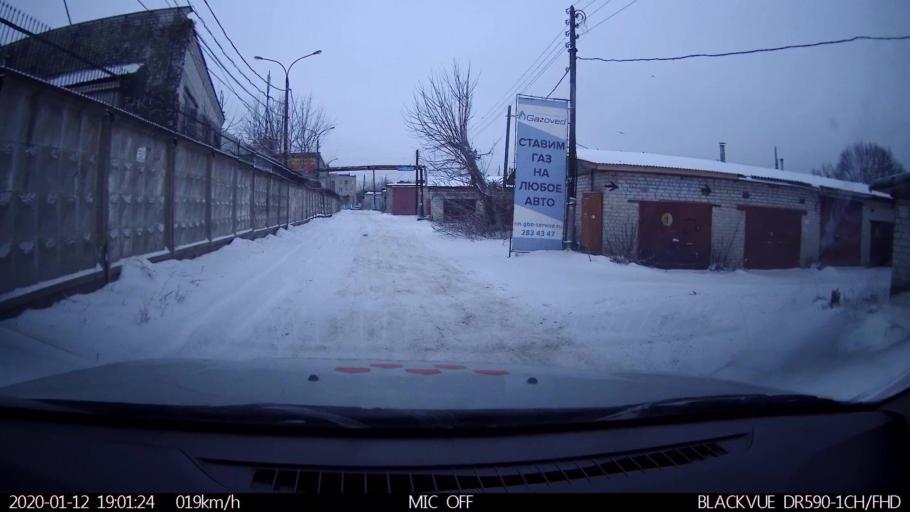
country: RU
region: Nizjnij Novgorod
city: Nizhniy Novgorod
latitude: 56.3322
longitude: 43.9083
